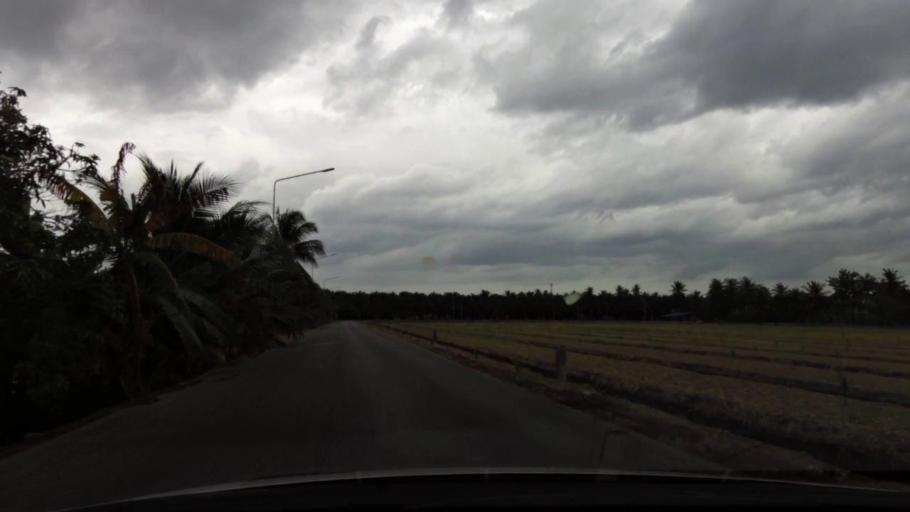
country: TH
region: Ratchaburi
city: Damnoen Saduak
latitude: 13.5752
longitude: 99.9812
